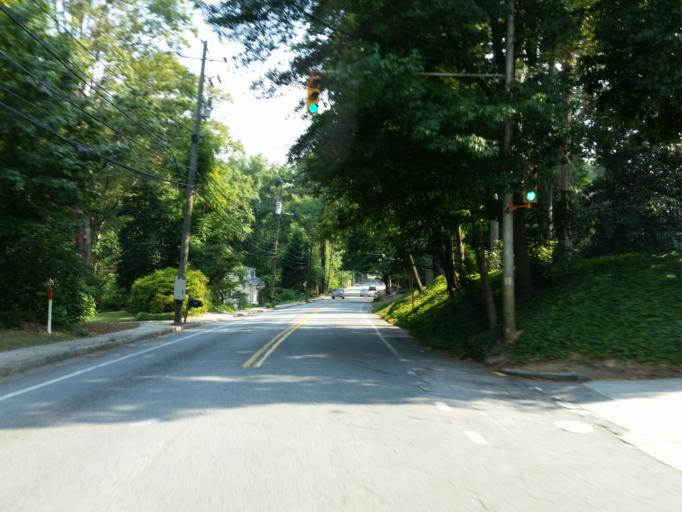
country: US
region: Georgia
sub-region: DeKalb County
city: North Atlanta
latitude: 33.8744
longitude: -84.3579
